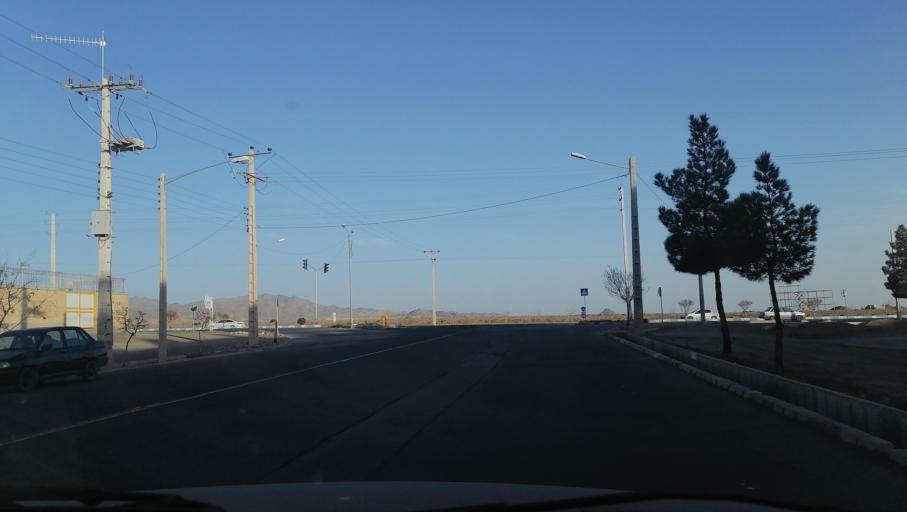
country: IR
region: Razavi Khorasan
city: Sabzevar
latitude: 36.2857
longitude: 57.6820
